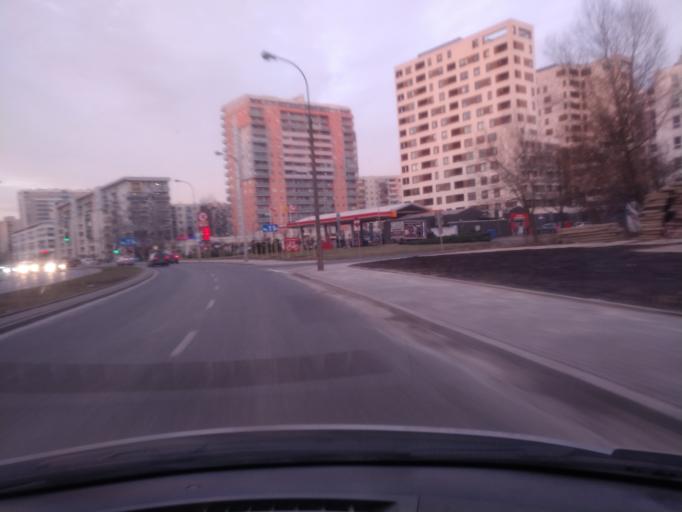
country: PL
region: Masovian Voivodeship
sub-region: Warszawa
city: Praga Poludnie
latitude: 52.2209
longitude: 21.0901
